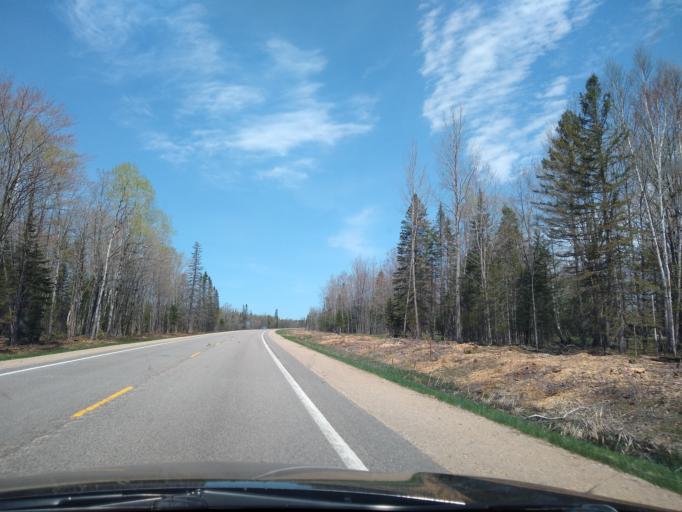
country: US
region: Michigan
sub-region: Delta County
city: Gladstone
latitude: 46.0319
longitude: -86.9802
